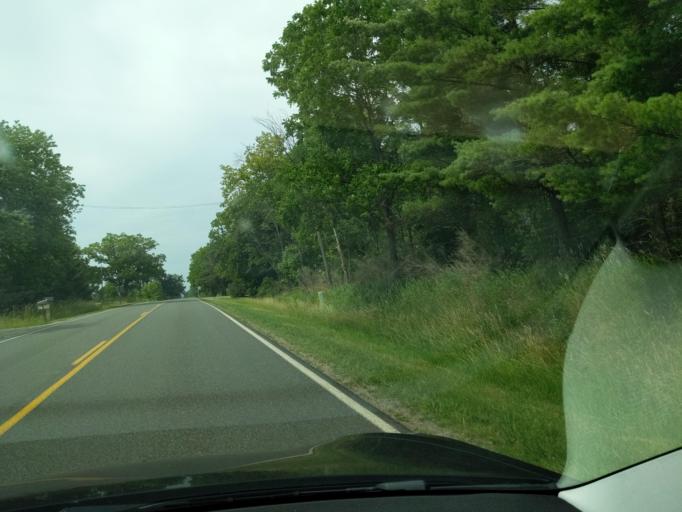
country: US
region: Michigan
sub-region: Clinton County
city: DeWitt
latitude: 42.8846
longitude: -84.6023
